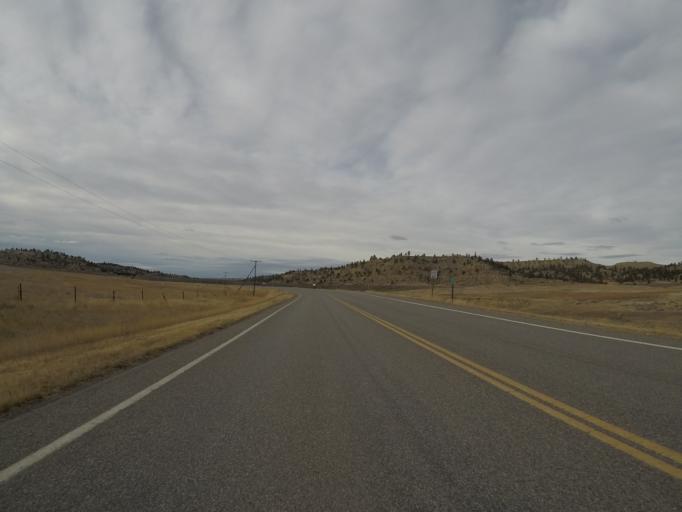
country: US
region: Montana
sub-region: Yellowstone County
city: Laurel
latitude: 45.8155
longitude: -108.6825
